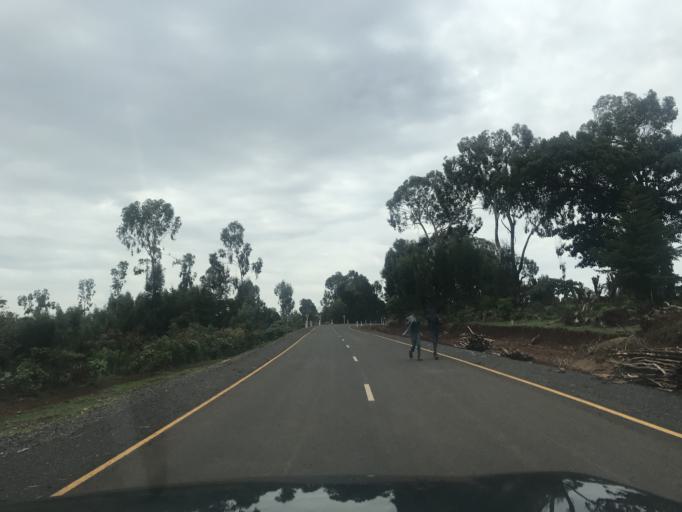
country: ET
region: Oromiya
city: Shambu
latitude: 9.8868
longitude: 36.6634
